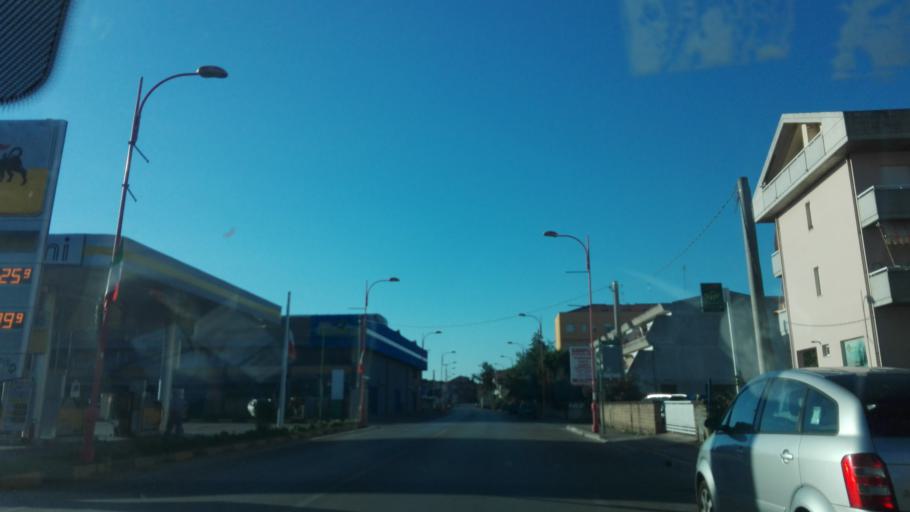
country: IT
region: Abruzzo
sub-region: Provincia di Pescara
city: Montesilvano Marina
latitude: 42.5046
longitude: 14.1619
